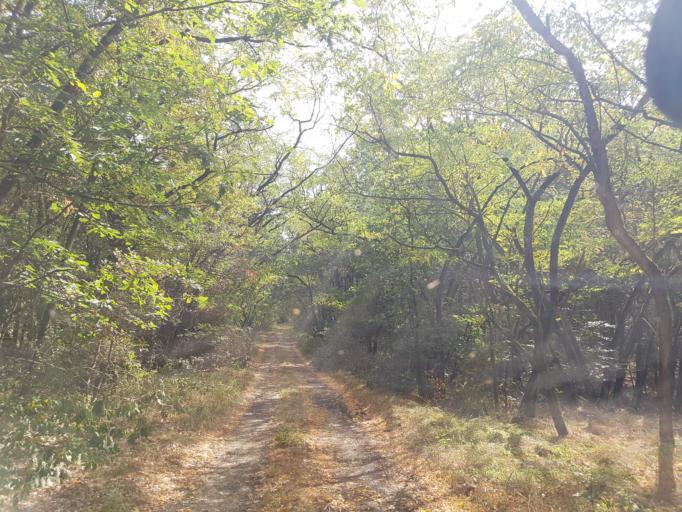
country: DE
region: Brandenburg
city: Finsterwalde
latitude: 51.5961
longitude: 13.7364
